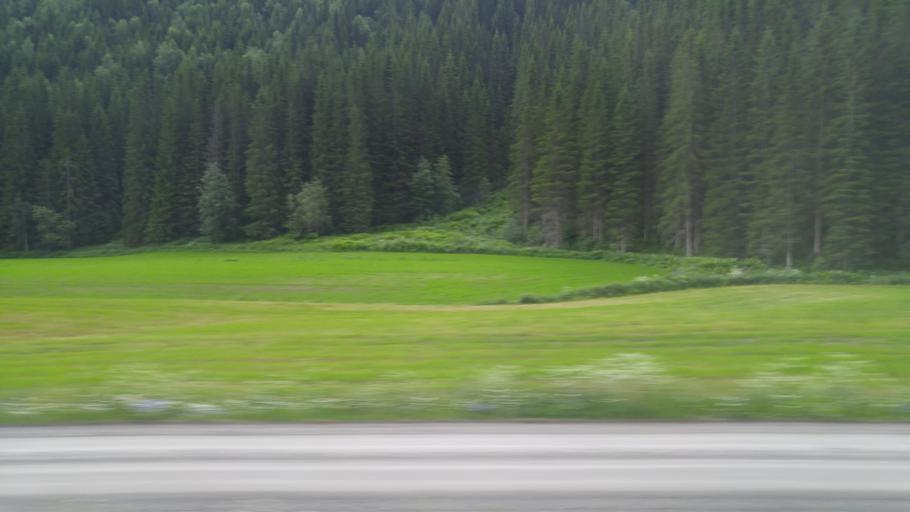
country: NO
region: Nord-Trondelag
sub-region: Levanger
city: Levanger
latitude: 63.4576
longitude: 11.3767
